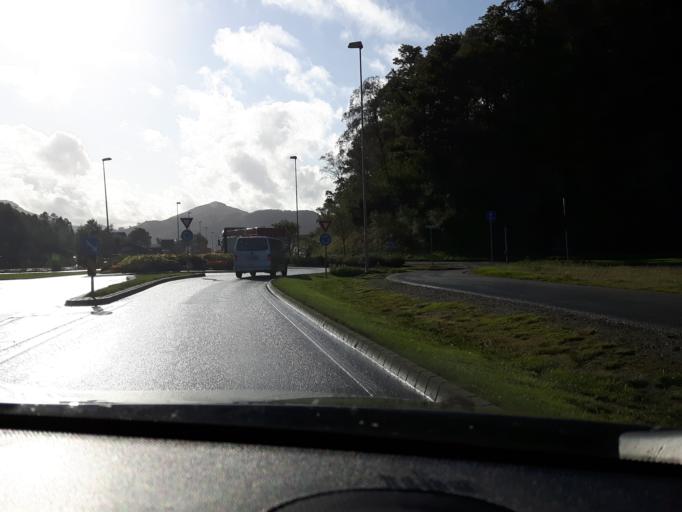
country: NO
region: Rogaland
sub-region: Gjesdal
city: Algard
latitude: 58.7694
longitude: 5.8563
